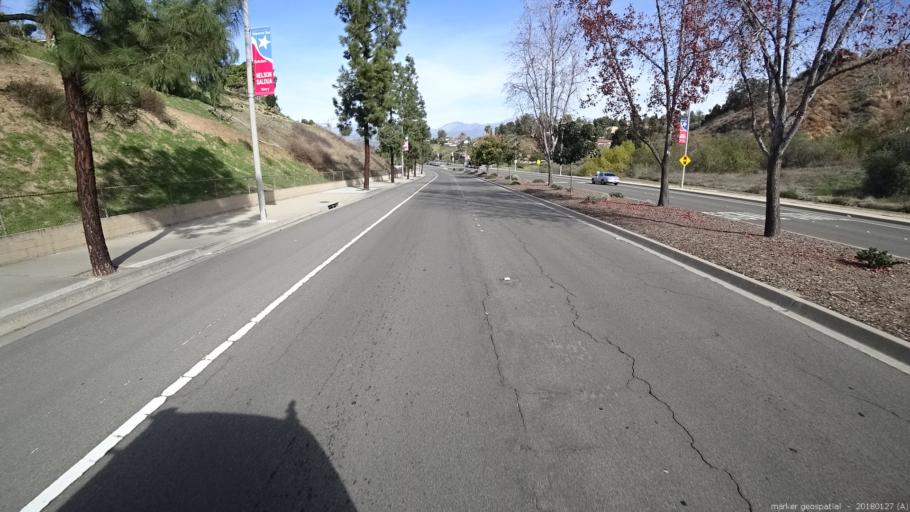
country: US
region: California
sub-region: Los Angeles County
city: Diamond Bar
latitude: 34.0126
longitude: -117.8073
